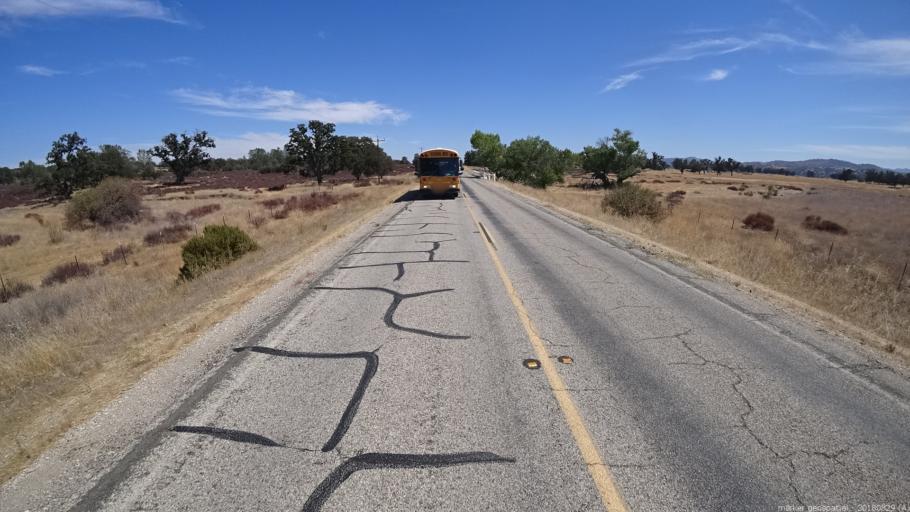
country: US
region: California
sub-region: Monterey County
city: King City
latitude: 35.9664
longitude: -121.1731
